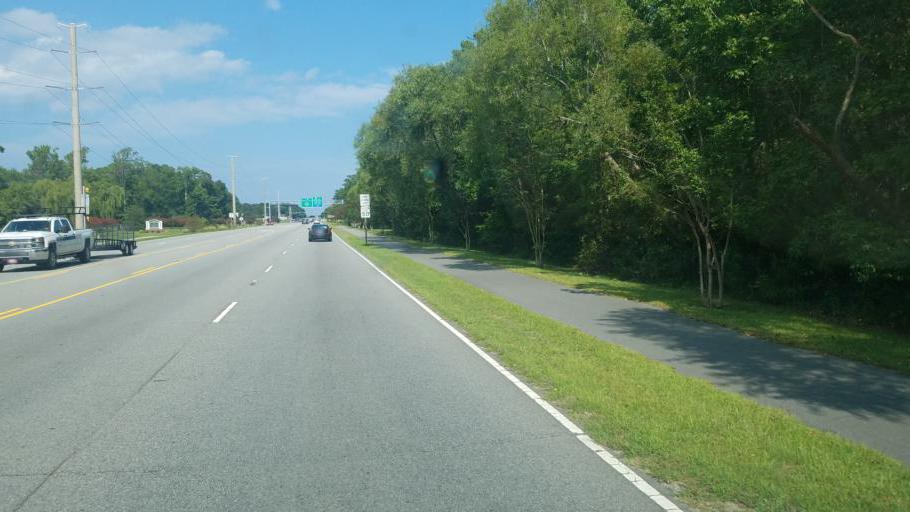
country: US
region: North Carolina
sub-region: Dare County
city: Kitty Hawk
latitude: 36.0963
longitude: -75.7305
